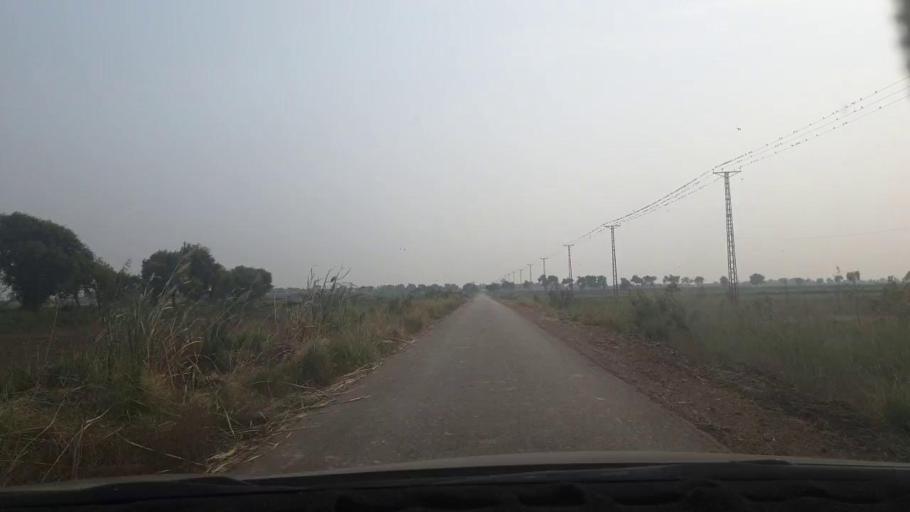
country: PK
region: Sindh
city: Jamshoro
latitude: 25.5152
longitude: 68.3145
